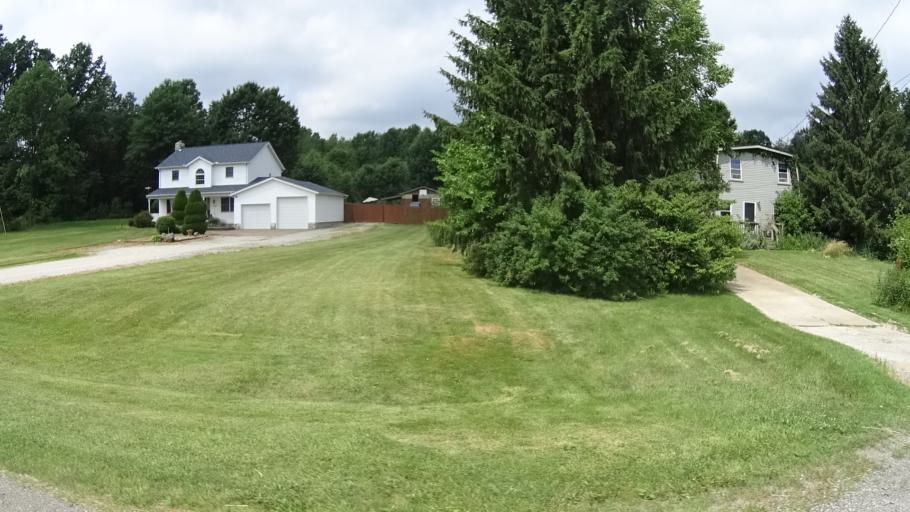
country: US
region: Ohio
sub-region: Lorain County
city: Vermilion
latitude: 41.3759
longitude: -82.3638
